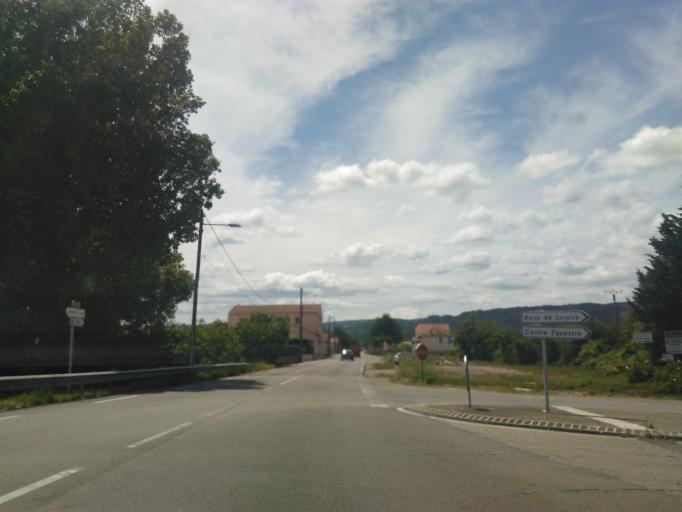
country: FR
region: Rhone-Alpes
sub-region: Departement de l'Ardeche
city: Le Teil
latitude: 44.5536
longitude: 4.7108
